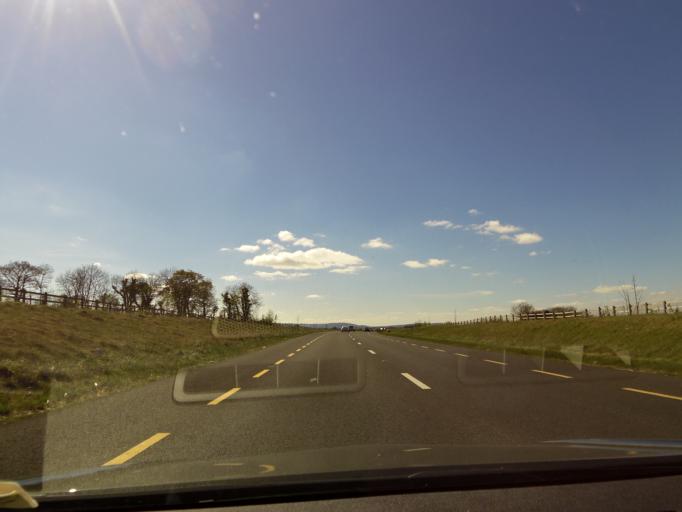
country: IE
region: Leinster
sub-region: Kildare
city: Athy
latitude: 52.9863
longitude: -6.9302
